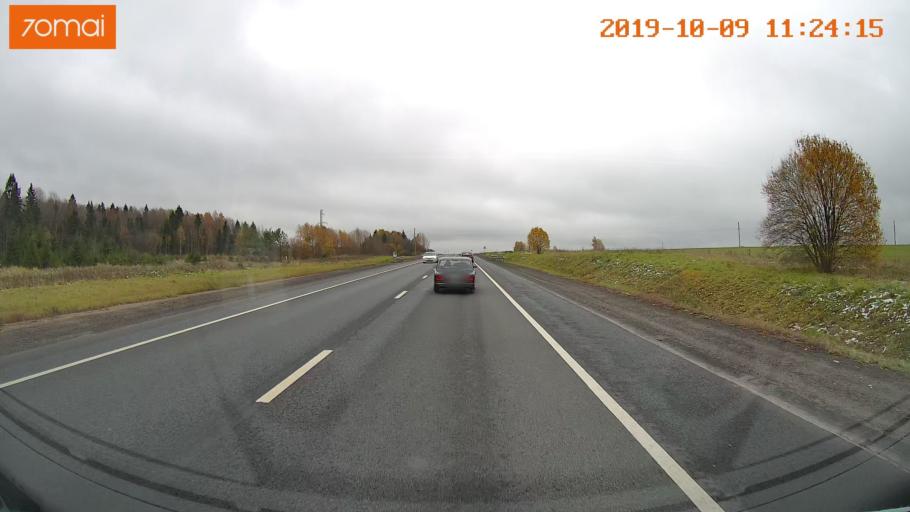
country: RU
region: Vologda
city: Vologda
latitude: 59.1132
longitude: 39.9781
